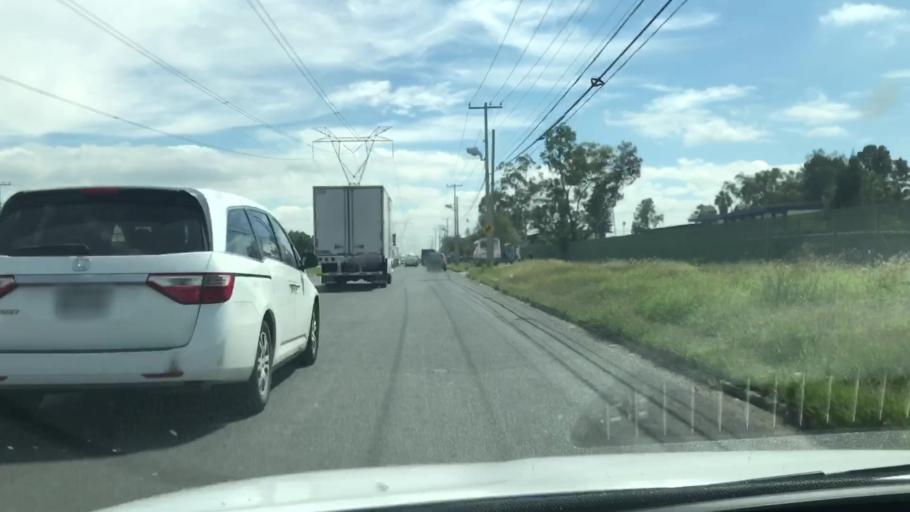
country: MX
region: Guanajuato
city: Celaya
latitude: 20.5515
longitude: -100.8131
